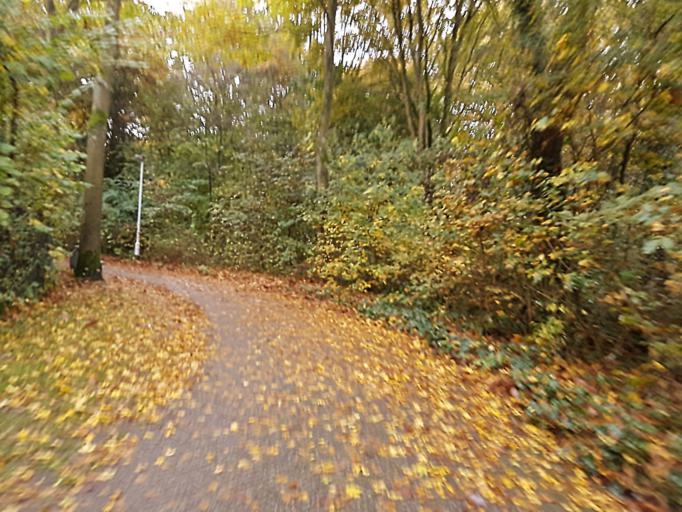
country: BE
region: Flanders
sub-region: Provincie Antwerpen
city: Hove
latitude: 51.1506
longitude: 4.4736
